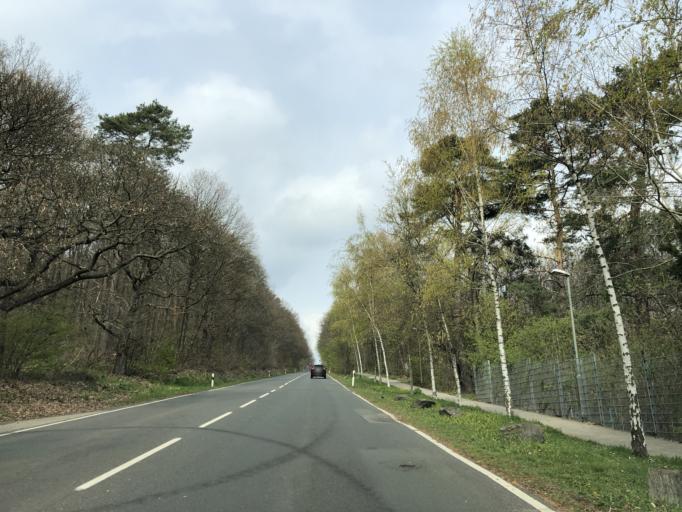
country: DE
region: Hesse
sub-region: Regierungsbezirk Darmstadt
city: Konigstein im Taunus
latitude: 50.1615
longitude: 8.4850
